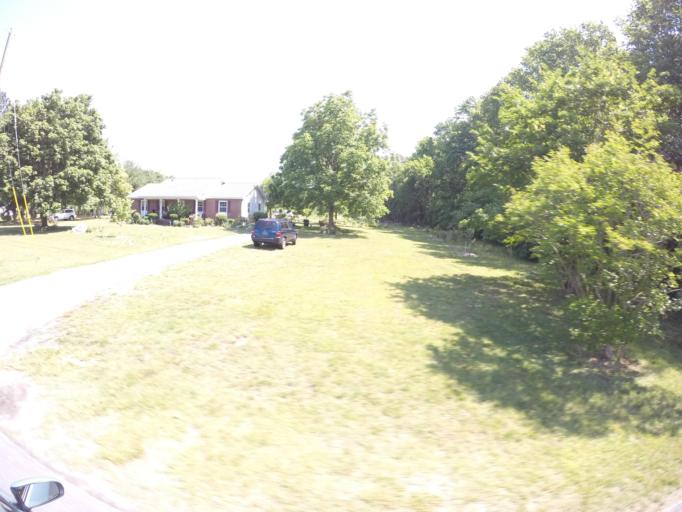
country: US
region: Delaware
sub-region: Sussex County
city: Georgetown
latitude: 38.6963
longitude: -75.3647
